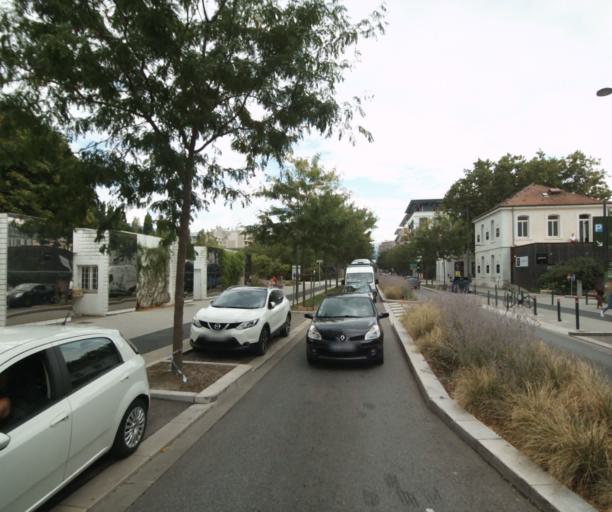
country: FR
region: Rhone-Alpes
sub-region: Departement de l'Isere
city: Grenoble
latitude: 45.1846
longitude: 5.7257
